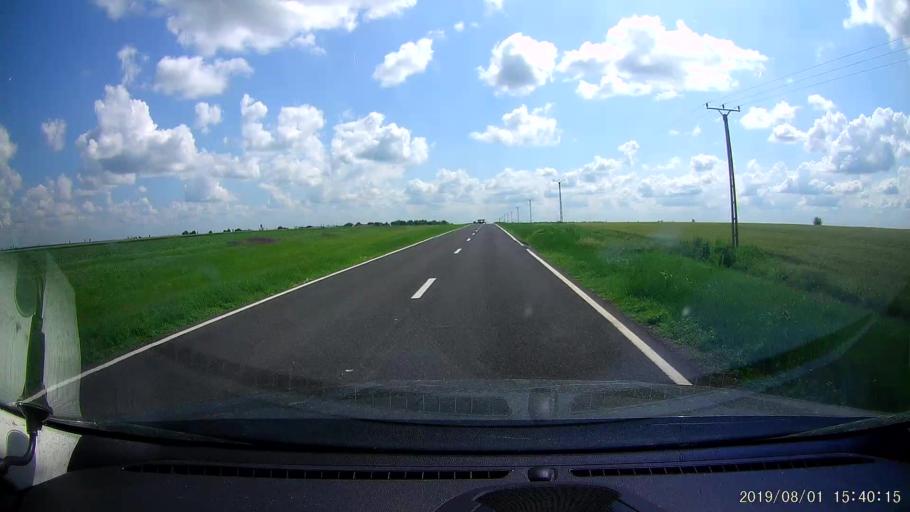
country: RO
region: Braila
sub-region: Comuna Baraganul
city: Baraganul
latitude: 44.8409
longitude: 27.5455
